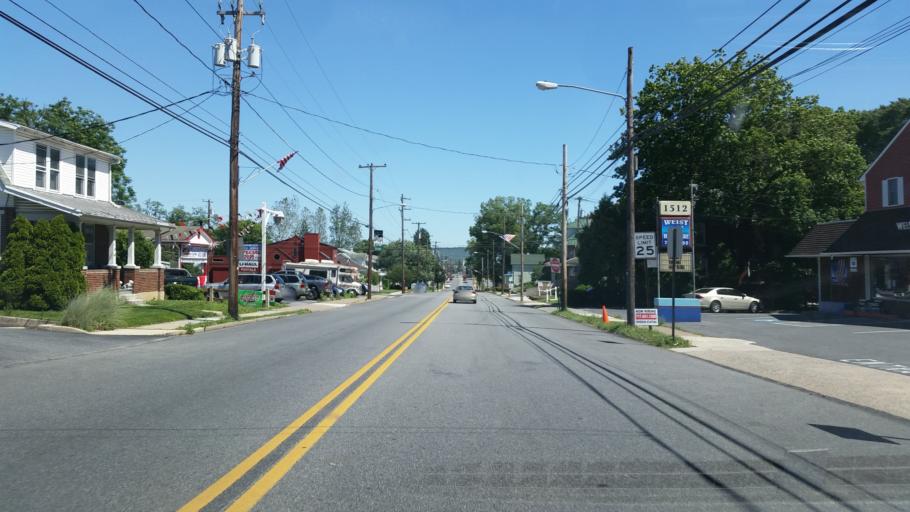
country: US
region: Pennsylvania
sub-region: Cumberland County
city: New Cumberland
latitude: 40.2357
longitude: -76.8777
